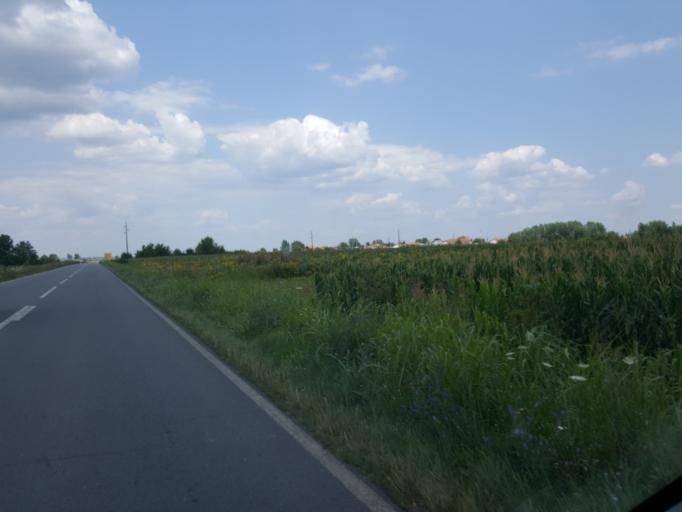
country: RS
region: Autonomna Pokrajina Vojvodina
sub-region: Sremski Okrug
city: Pecinci
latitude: 44.9118
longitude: 19.9566
